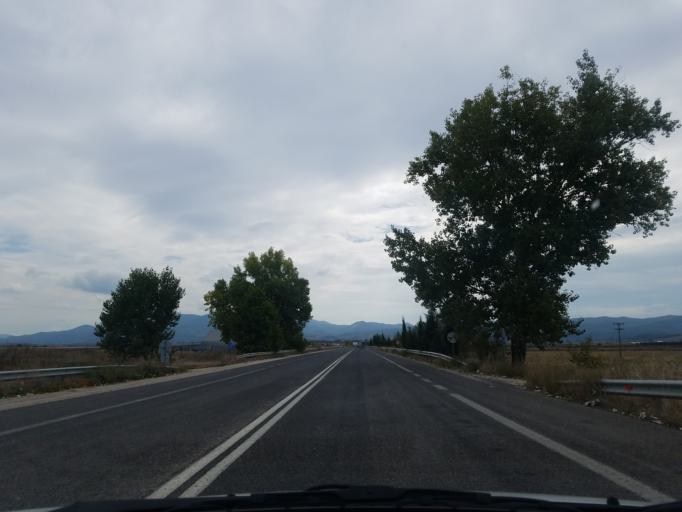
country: GR
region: Central Greece
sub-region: Nomos Fthiotidos
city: Omvriaki
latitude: 39.0738
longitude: 22.3188
